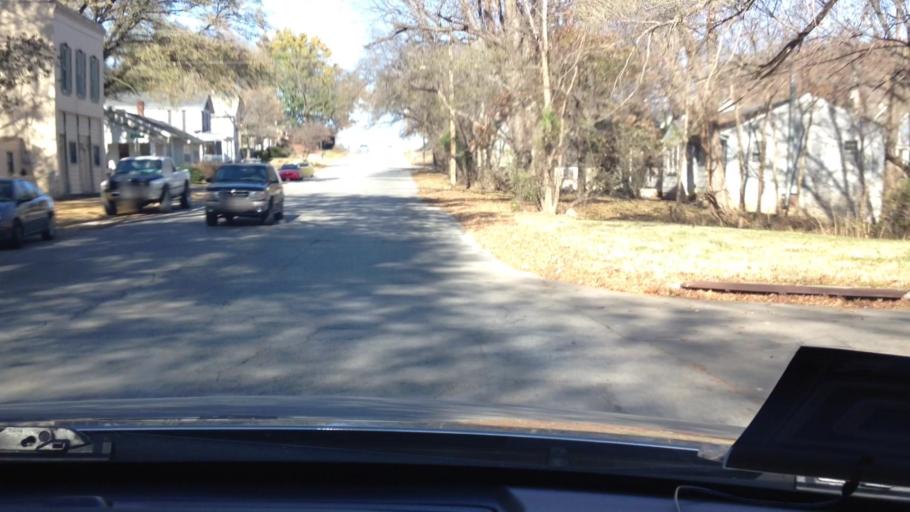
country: US
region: Kansas
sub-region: Leavenworth County
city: Leavenworth
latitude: 39.3058
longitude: -94.9136
